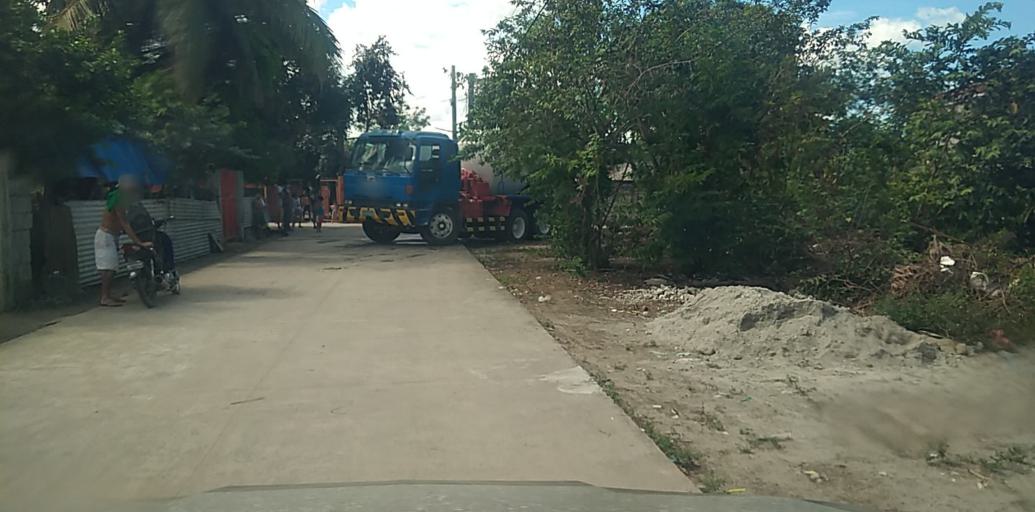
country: PH
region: Central Luzon
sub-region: Province of Pampanga
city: Buensuseso
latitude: 15.1925
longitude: 120.6691
